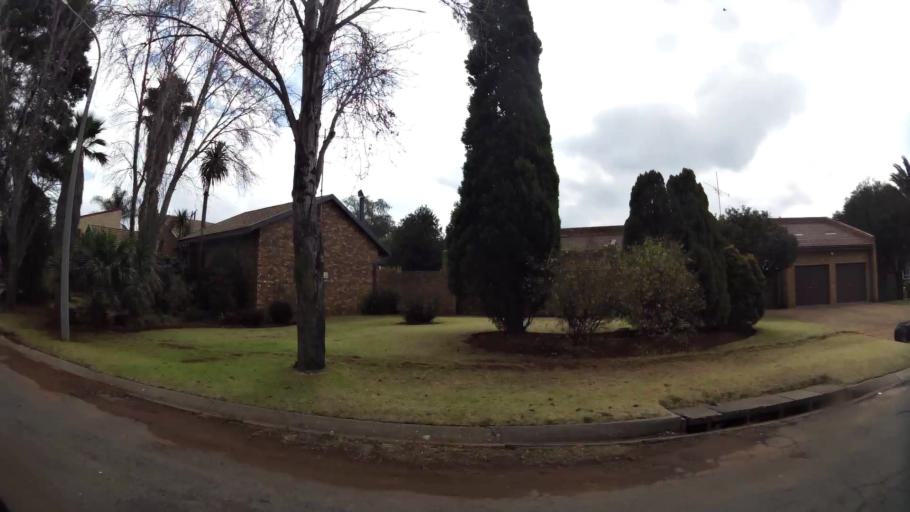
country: ZA
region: Gauteng
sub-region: Sedibeng District Municipality
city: Vanderbijlpark
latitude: -26.7405
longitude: 27.8500
